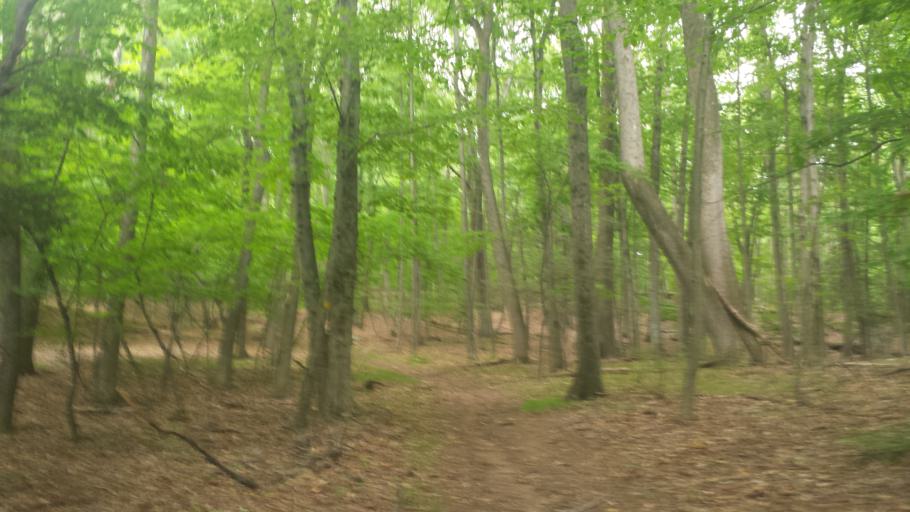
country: US
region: New York
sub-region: Westchester County
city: Croton-on-Hudson
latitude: 41.2249
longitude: -73.8289
